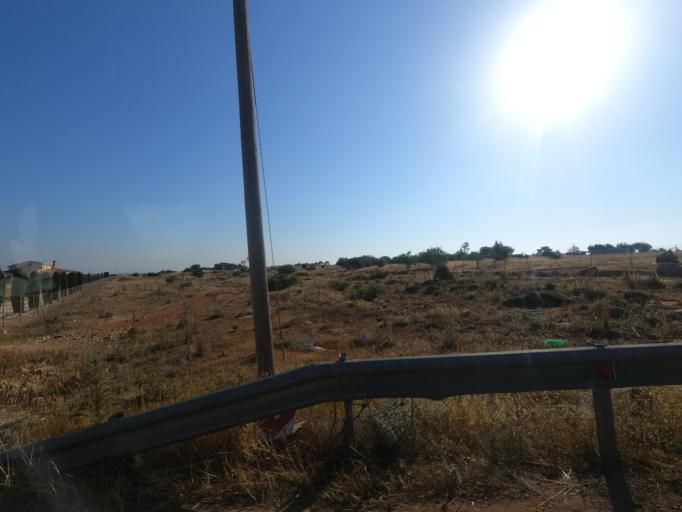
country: CY
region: Ammochostos
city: Frenaros
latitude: 35.0603
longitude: 33.9064
